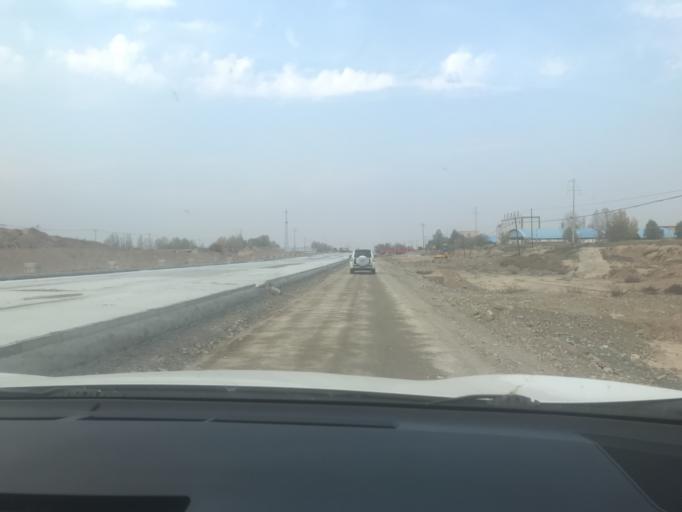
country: CN
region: Gansu Sheng
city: Gulang
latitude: 37.5123
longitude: 102.9010
